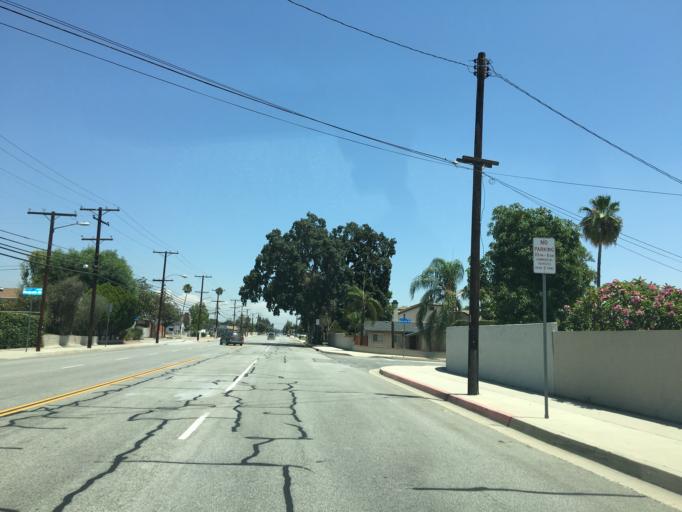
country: US
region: California
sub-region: Los Angeles County
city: Charter Oak
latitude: 34.1030
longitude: -117.8605
